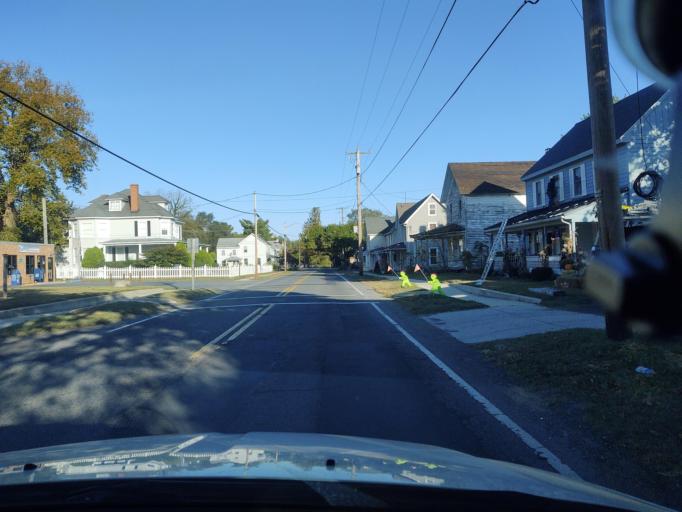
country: US
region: Maryland
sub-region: Queen Anne's County
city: Kingstown
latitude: 39.2403
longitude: -75.9212
